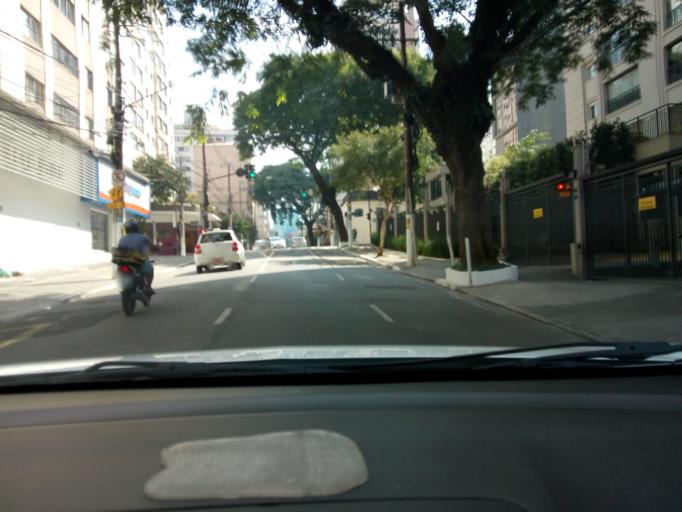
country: BR
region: Sao Paulo
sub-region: Sao Paulo
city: Sao Paulo
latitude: -23.5800
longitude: -46.6418
